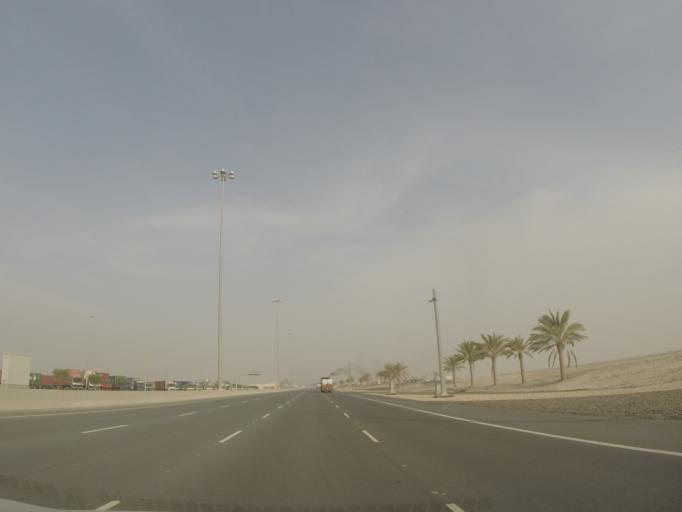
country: AE
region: Abu Dhabi
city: Abu Dhabi
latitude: 24.7802
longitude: 54.7057
